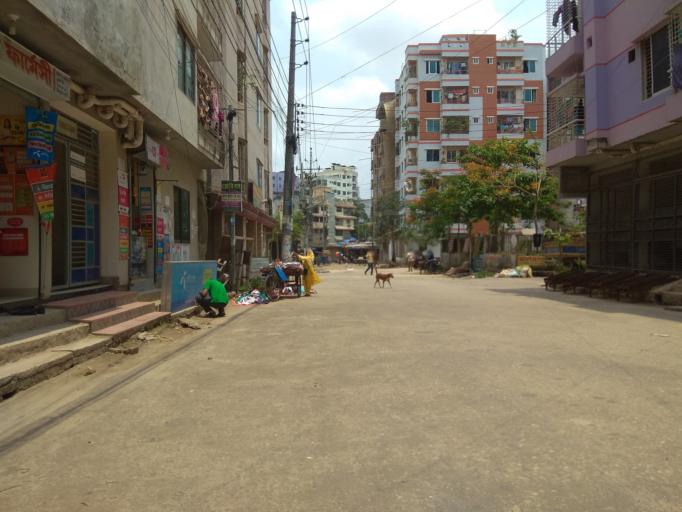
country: BD
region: Dhaka
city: Azimpur
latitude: 23.8103
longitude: 90.3749
